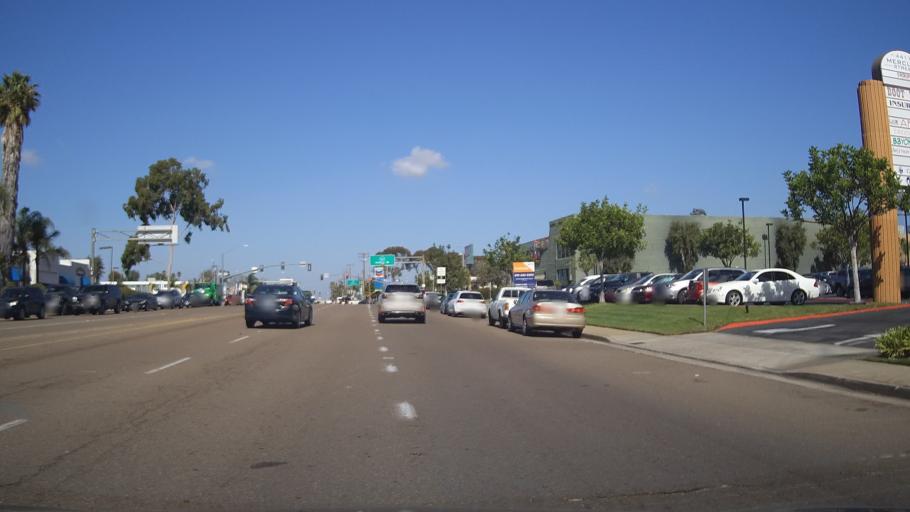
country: US
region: California
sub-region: San Diego County
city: San Diego
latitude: 32.8203
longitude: -117.1490
